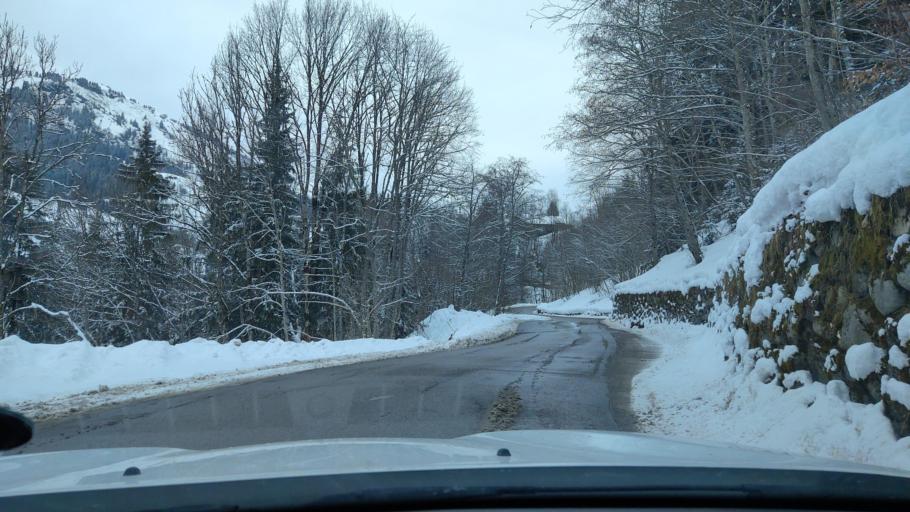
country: FR
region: Rhone-Alpes
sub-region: Departement de la Savoie
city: Beaufort
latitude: 45.7470
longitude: 6.5901
